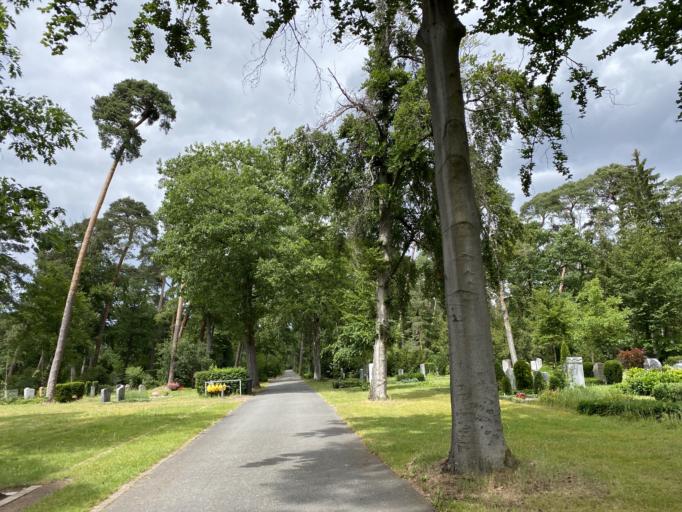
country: DE
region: Hesse
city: Griesheim
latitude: 49.8708
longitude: 8.6102
